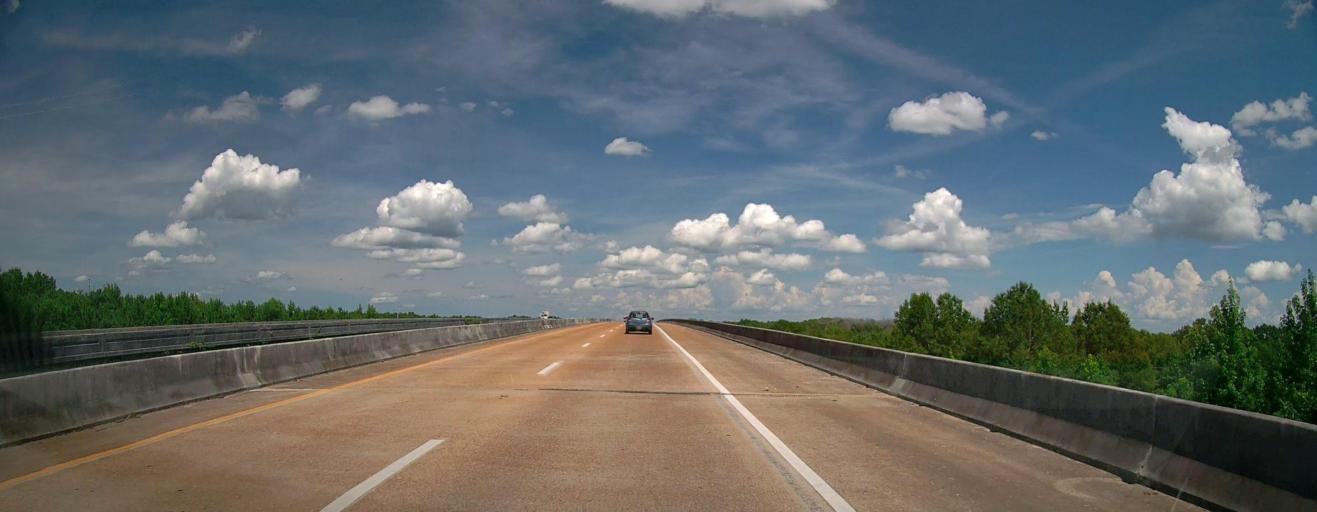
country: US
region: Mississippi
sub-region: Monroe County
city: Aberdeen
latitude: 33.8174
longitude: -88.5203
